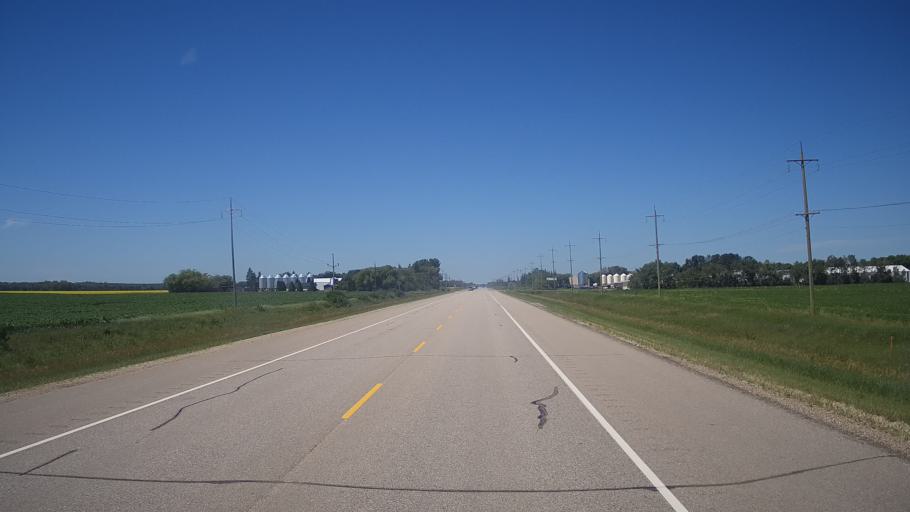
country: CA
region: Manitoba
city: Neepawa
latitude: 50.2252
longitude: -99.3122
